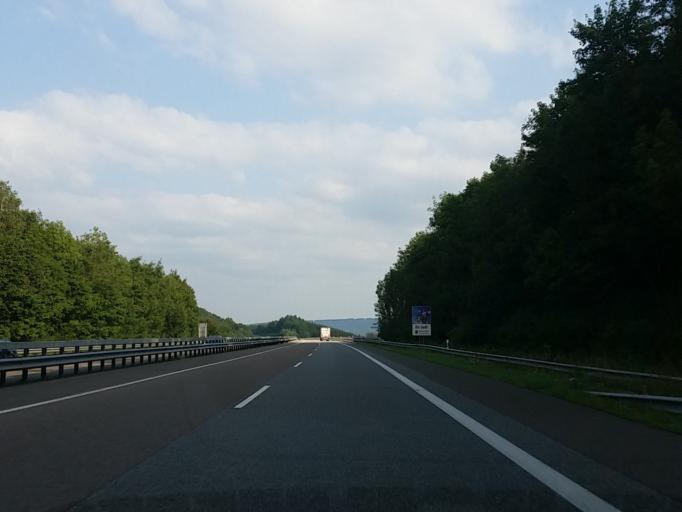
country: DE
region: Saarland
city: Nonnweiler
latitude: 49.6253
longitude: 6.9297
